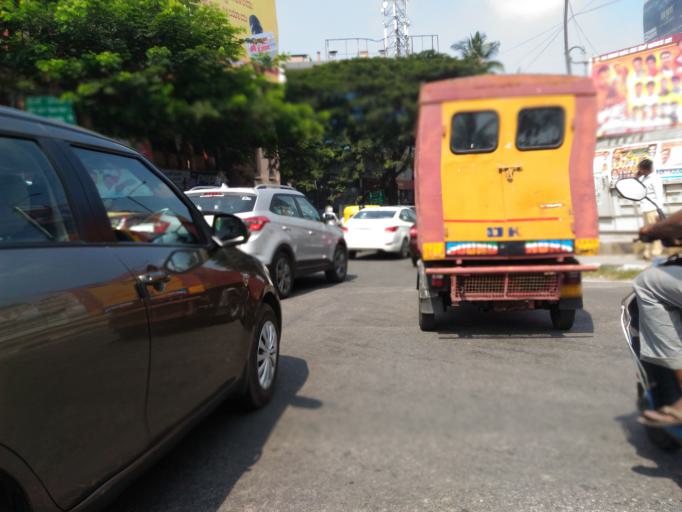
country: IN
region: Karnataka
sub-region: Bangalore Urban
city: Bangalore
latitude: 12.9552
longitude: 77.5798
